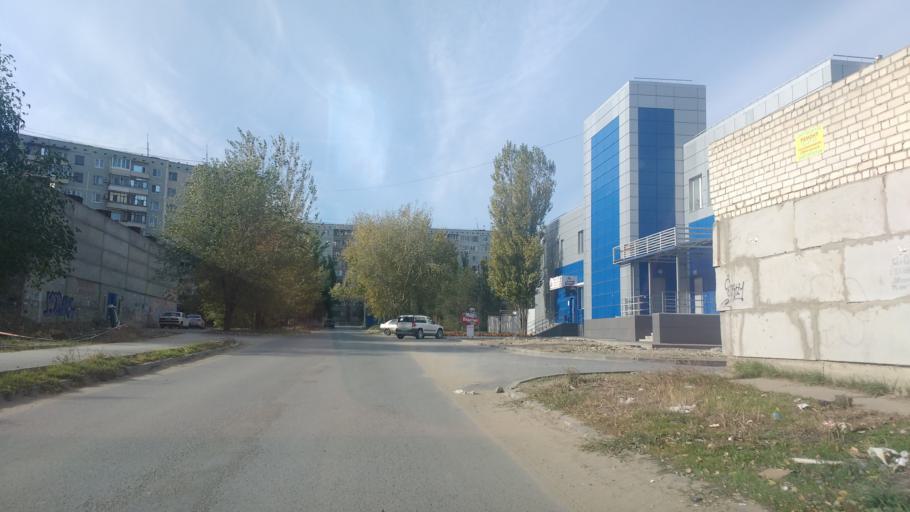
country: RU
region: Volgograd
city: Krasnoslobodsk
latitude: 48.7648
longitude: 44.5494
